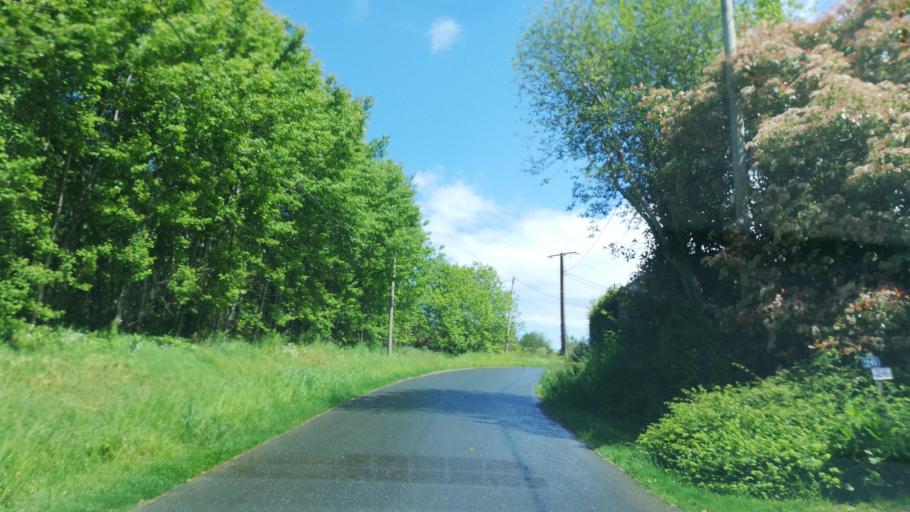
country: FR
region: Brittany
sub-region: Departement d'Ille-et-Vilaine
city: Irodouer
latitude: 48.2535
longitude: -1.9474
